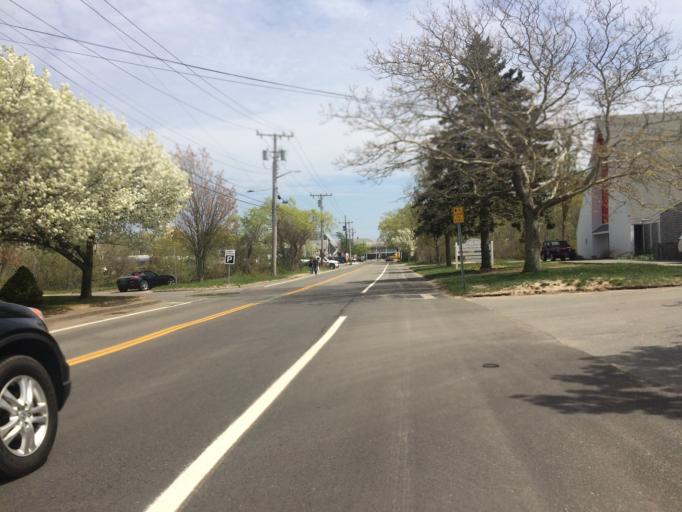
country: US
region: Massachusetts
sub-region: Barnstable County
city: Provincetown
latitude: 42.0492
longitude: -70.1939
